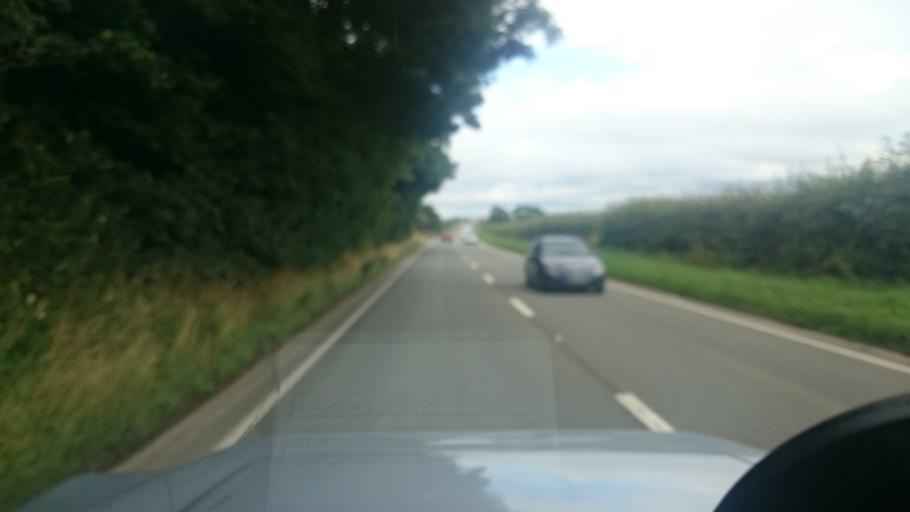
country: GB
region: Wales
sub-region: Pembrokeshire
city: Haverfordwest
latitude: 51.8062
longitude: -4.9358
